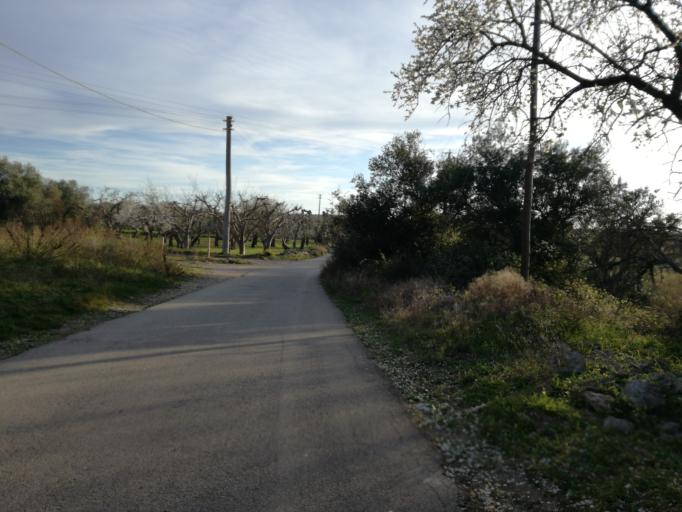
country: IT
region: Apulia
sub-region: Provincia di Bari
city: Valenzano
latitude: 41.0523
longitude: 16.8949
